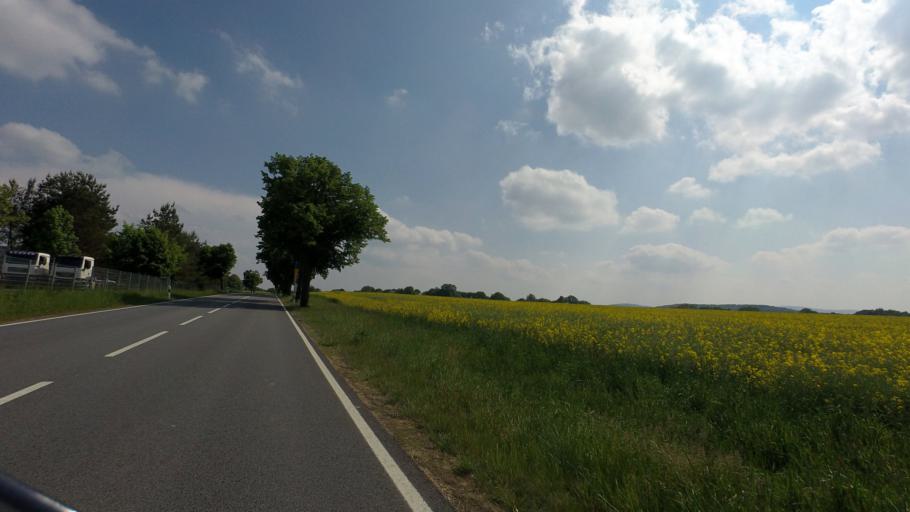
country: DE
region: Saxony
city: Weissenberg
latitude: 51.1957
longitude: 14.6704
